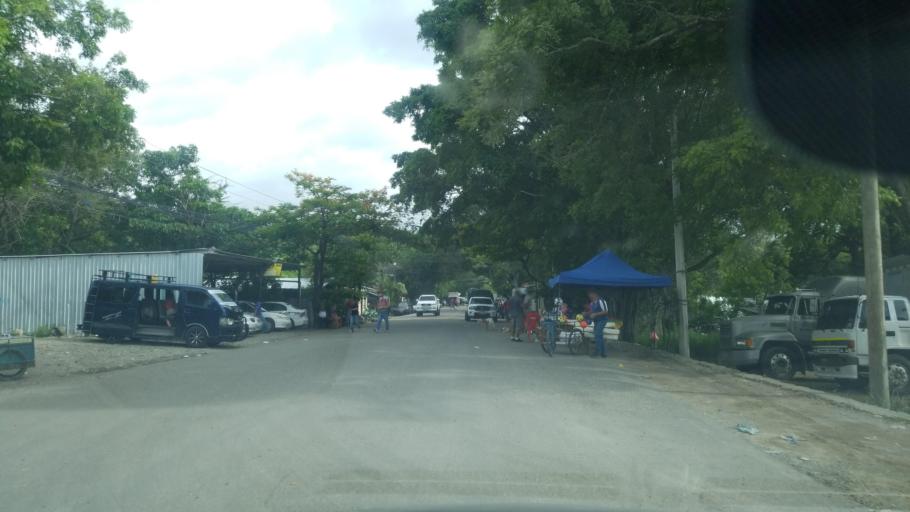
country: HN
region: Ocotepeque
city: Antigua Ocotepeque
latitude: 14.3759
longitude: -89.2092
